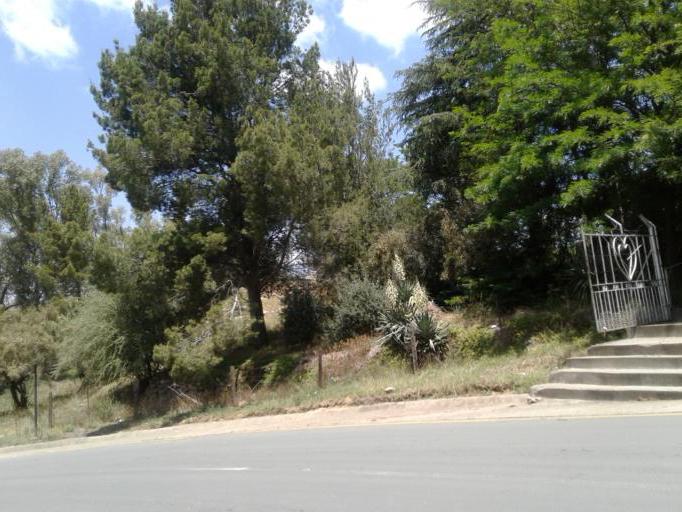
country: LS
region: Maseru
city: Maseru
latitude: -29.3097
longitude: 27.4829
